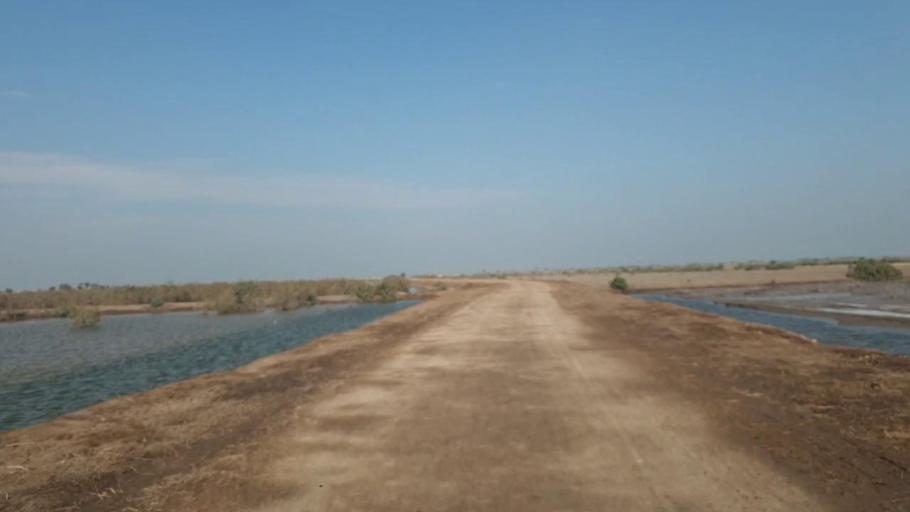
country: PK
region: Sindh
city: Shahdadpur
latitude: 25.9692
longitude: 68.5099
